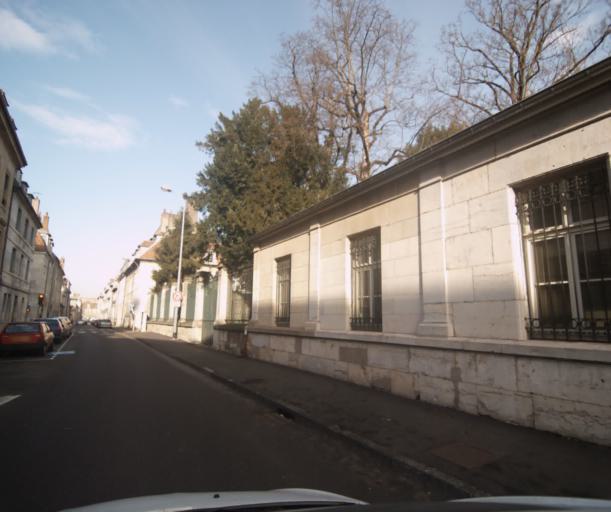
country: FR
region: Franche-Comte
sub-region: Departement du Doubs
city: Besancon
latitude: 47.2320
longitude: 6.0254
